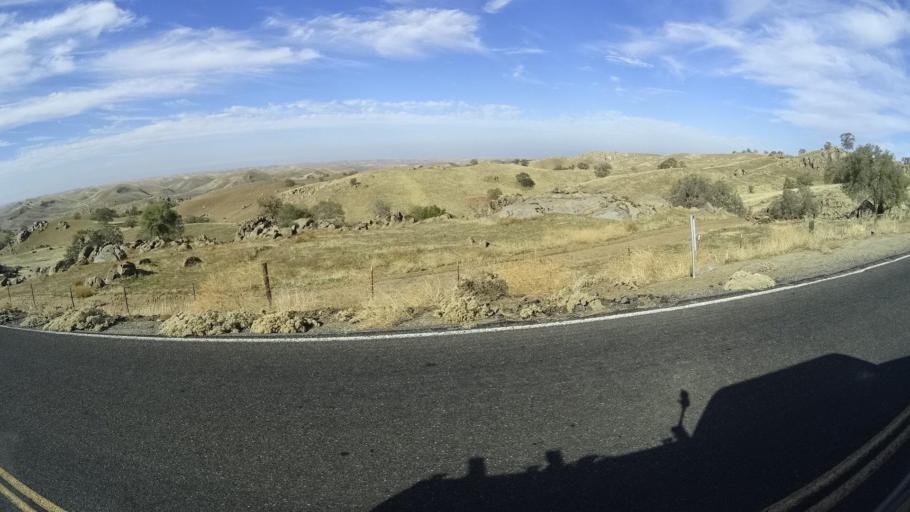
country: US
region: California
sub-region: Kern County
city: Oildale
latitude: 35.6189
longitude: -118.8566
